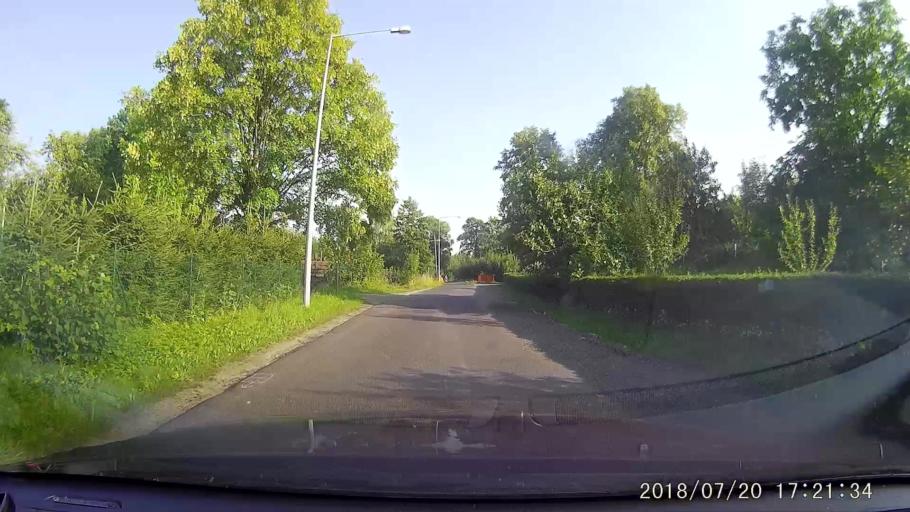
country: PL
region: Lower Silesian Voivodeship
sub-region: Powiat lubanski
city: Lesna
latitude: 50.9826
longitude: 15.2879
